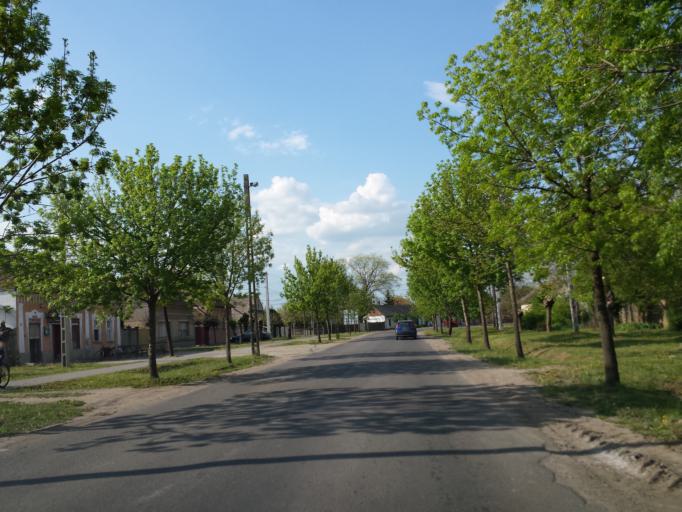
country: HU
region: Csongrad
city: Mako
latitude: 46.2340
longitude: 20.4801
